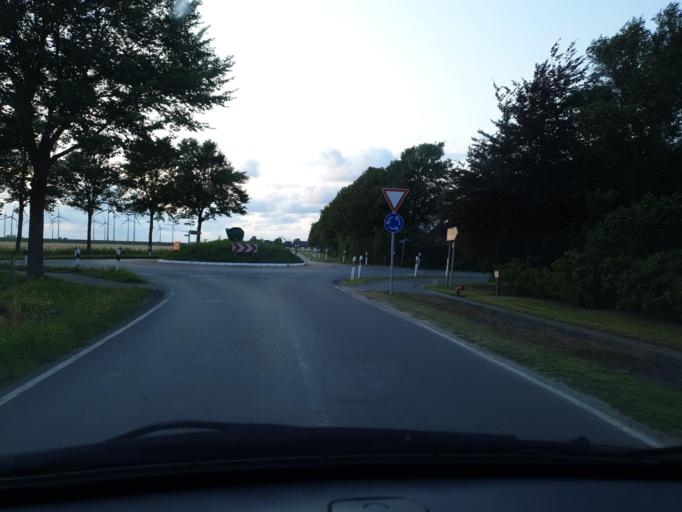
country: DE
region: Schleswig-Holstein
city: Kronprinzenkoog
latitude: 53.9466
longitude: 8.9404
